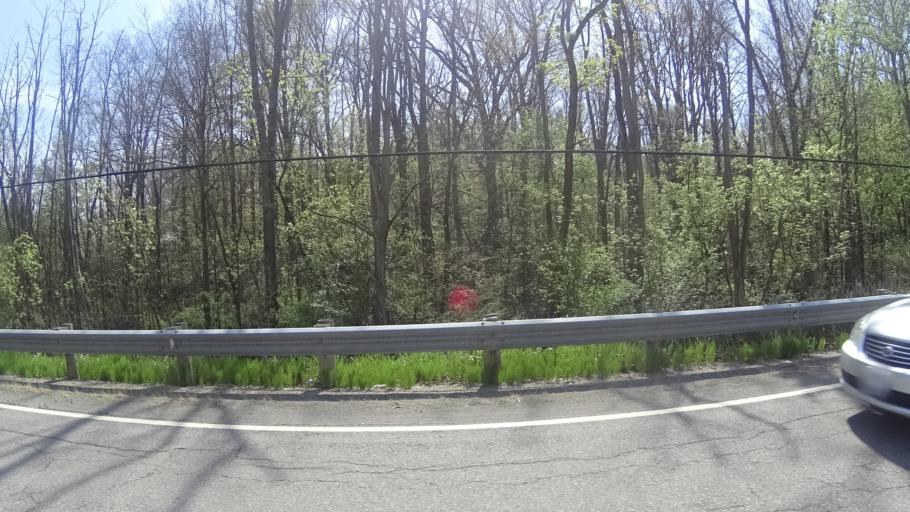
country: US
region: Ohio
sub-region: Lorain County
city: Lagrange
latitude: 41.2802
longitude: -82.1501
